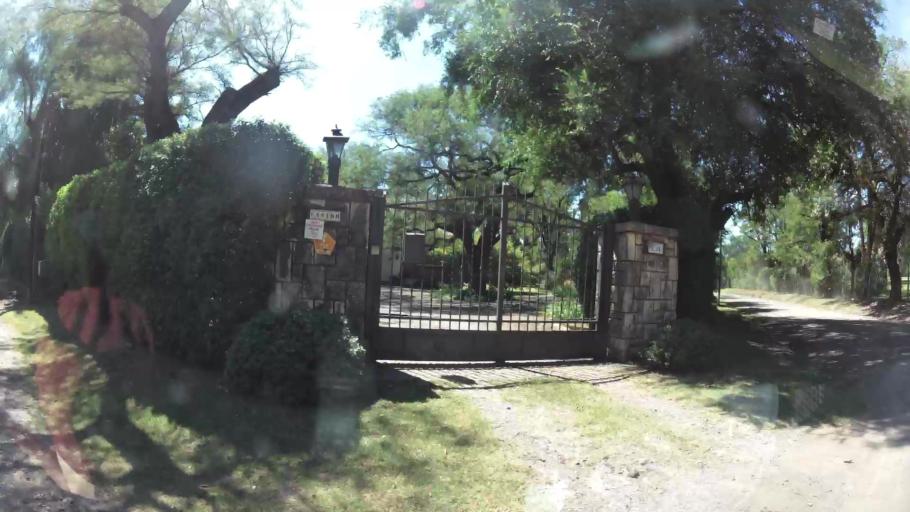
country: AR
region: Cordoba
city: Villa Allende
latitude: -31.2813
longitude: -64.2923
